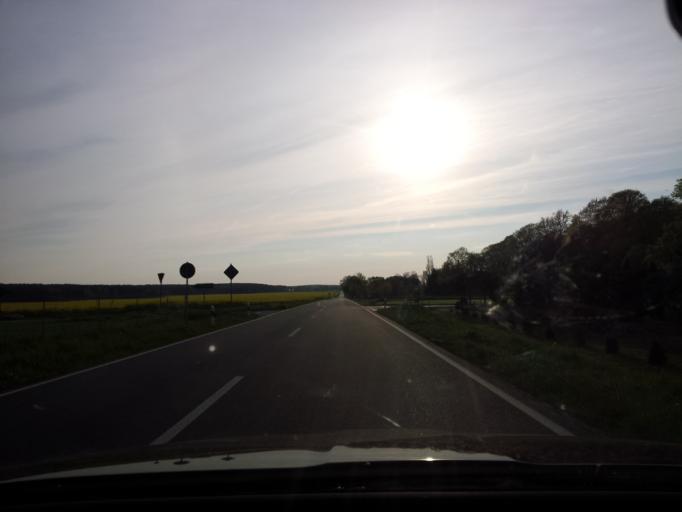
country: DE
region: Brandenburg
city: Drahnsdorf
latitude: 51.8492
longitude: 13.5666
